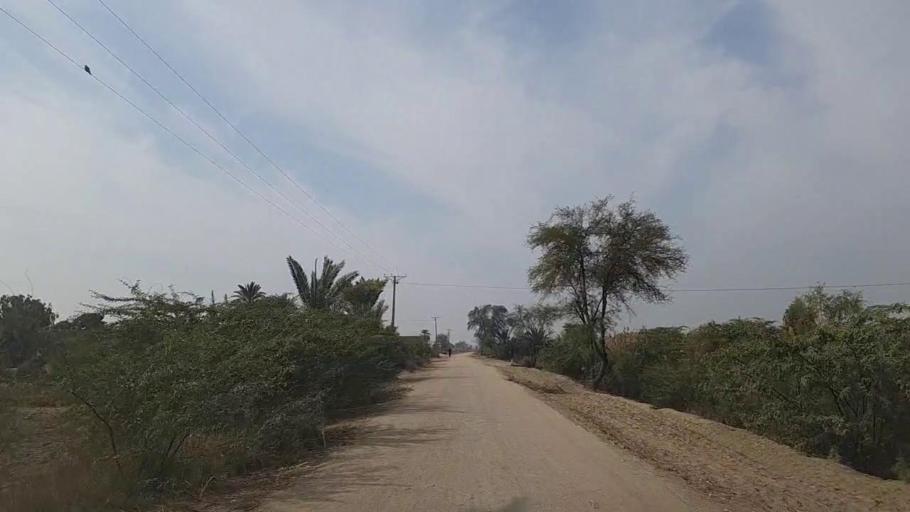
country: PK
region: Sindh
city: Daur
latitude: 26.4516
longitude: 68.4231
